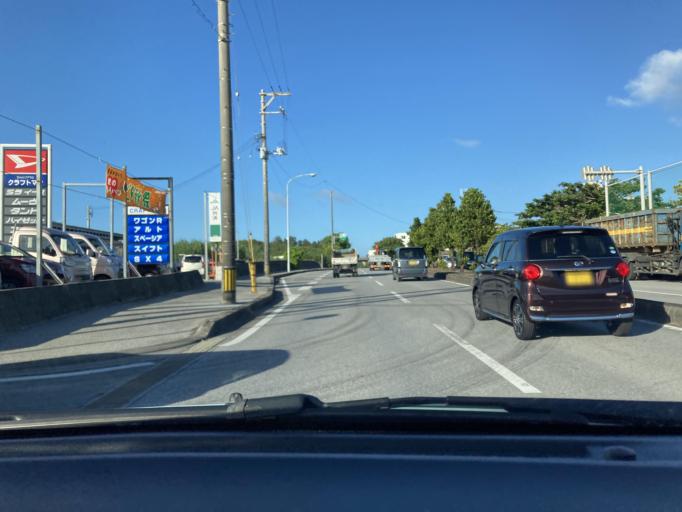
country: JP
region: Okinawa
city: Tomigusuku
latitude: 26.1727
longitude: 127.7109
